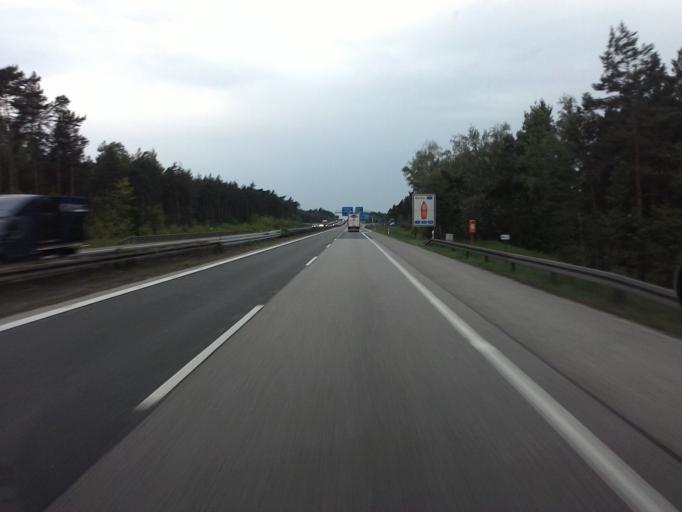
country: DE
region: Bavaria
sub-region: Regierungsbezirk Mittelfranken
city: Rothenbach an der Pegnitz
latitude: 49.4539
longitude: 11.2562
